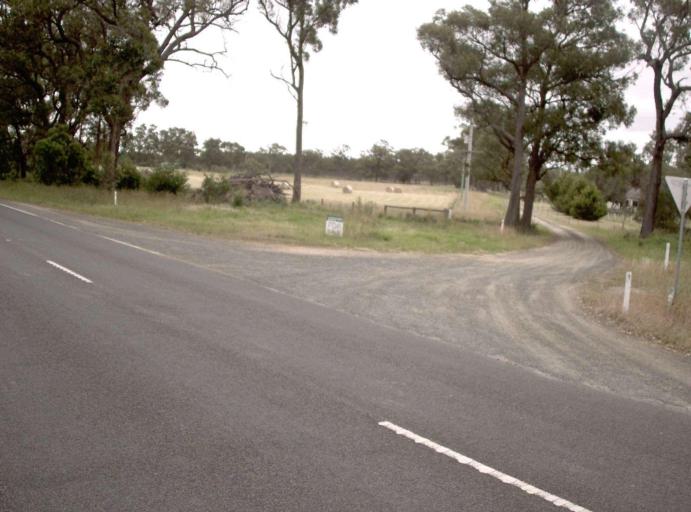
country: AU
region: Victoria
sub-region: Latrobe
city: Traralgon
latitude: -38.5292
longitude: 146.8649
